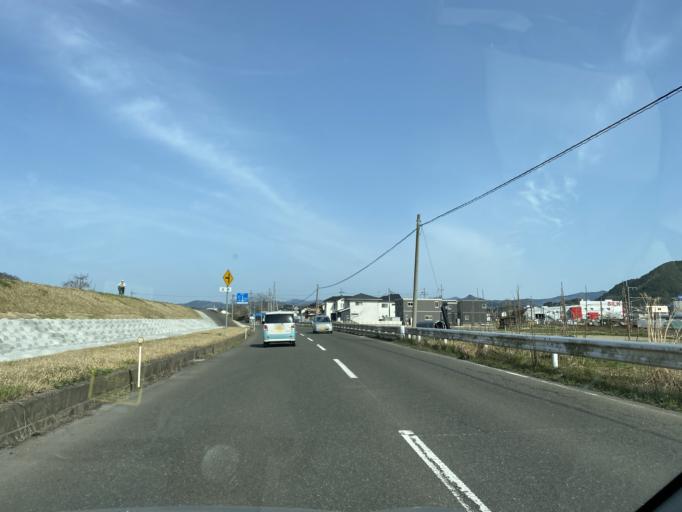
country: JP
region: Kyoto
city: Ayabe
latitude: 35.3048
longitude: 135.2274
